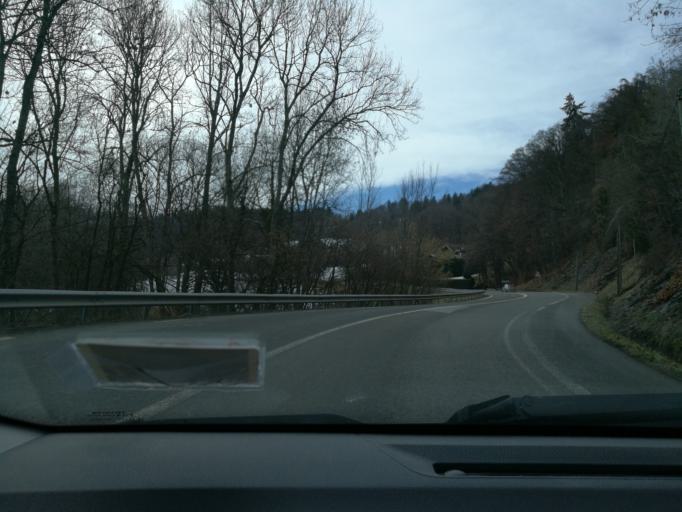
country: FR
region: Rhone-Alpes
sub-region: Departement de la Haute-Savoie
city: Domancy
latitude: 45.9164
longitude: 6.6364
